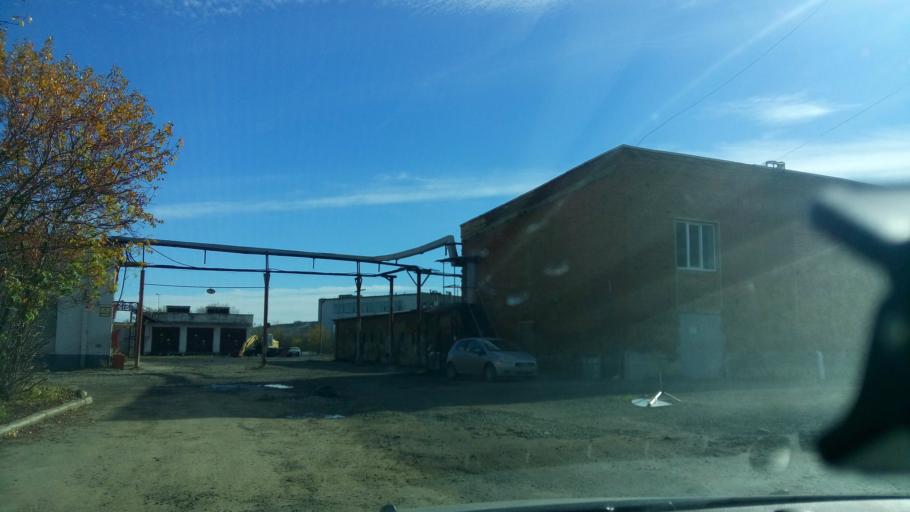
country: RU
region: Sverdlovsk
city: Sovkhoznyy
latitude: 56.7776
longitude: 60.6141
